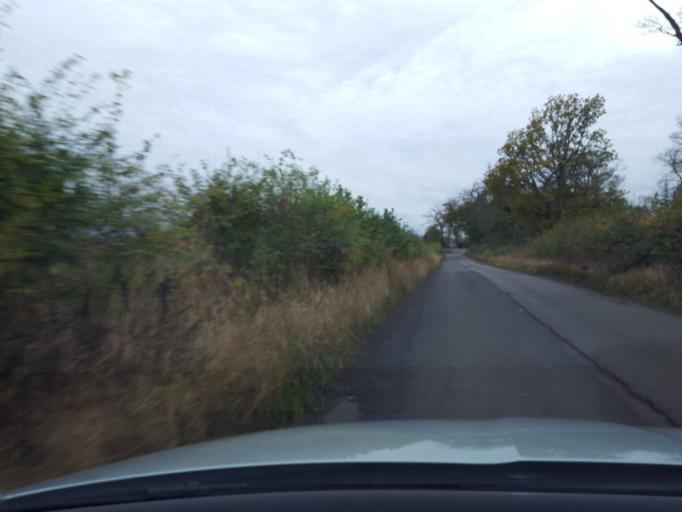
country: GB
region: Scotland
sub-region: Edinburgh
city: Ratho
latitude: 55.9178
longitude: -3.3656
